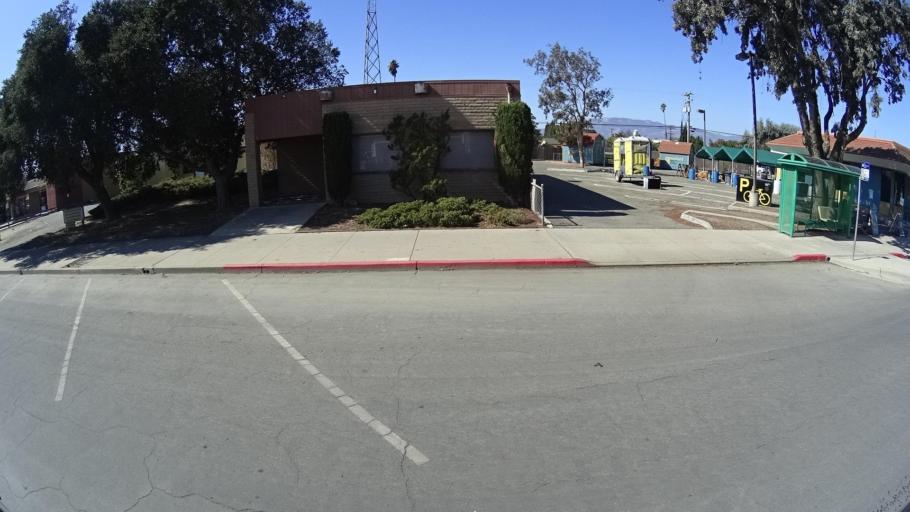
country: US
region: California
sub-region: Monterey County
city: Greenfield
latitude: 36.3190
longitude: -121.2417
